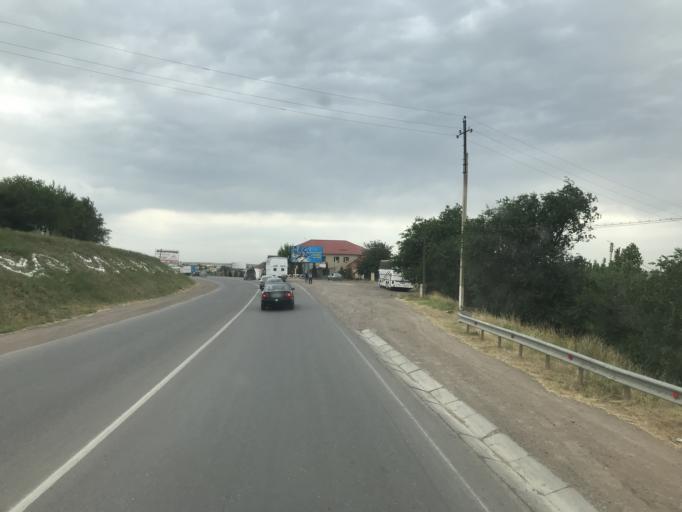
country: KZ
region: Ongtustik Qazaqstan
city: Saryaghash
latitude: 41.4585
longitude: 69.1415
